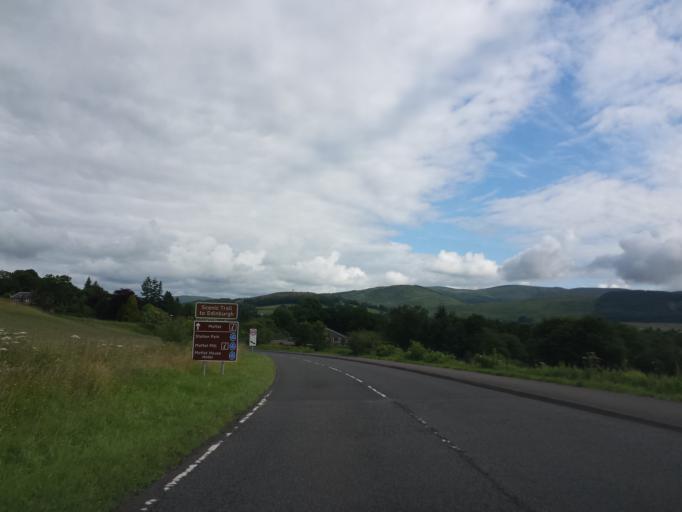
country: GB
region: Scotland
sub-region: Dumfries and Galloway
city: Moffat
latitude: 55.3200
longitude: -3.4453
